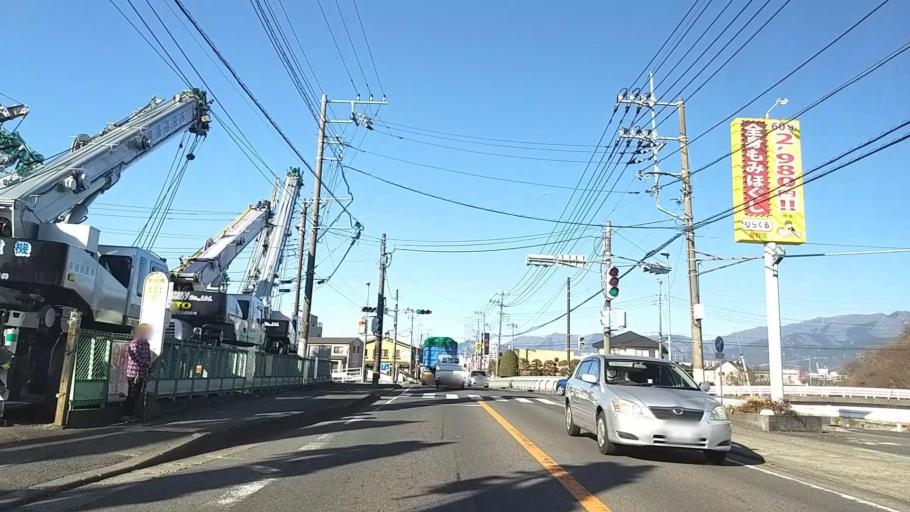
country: JP
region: Kanagawa
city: Hadano
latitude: 35.3678
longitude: 139.2395
